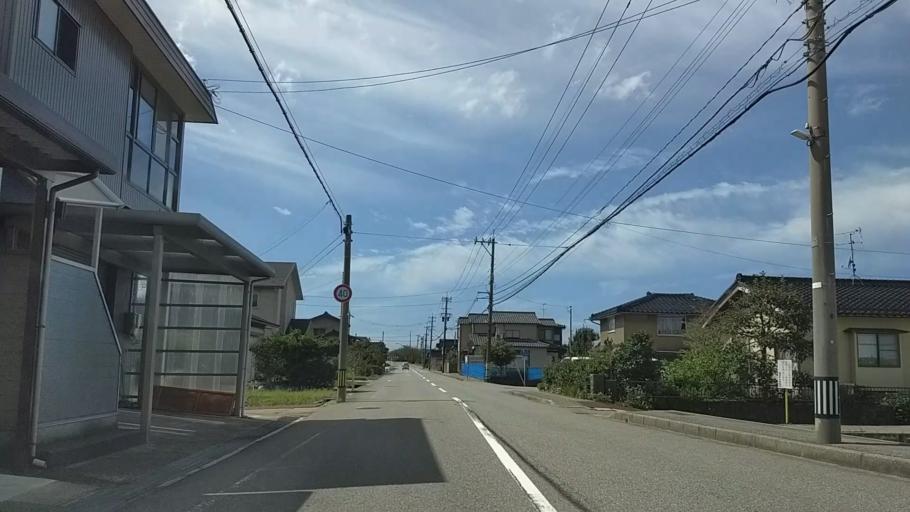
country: JP
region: Ishikawa
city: Kanazawa-shi
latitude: 36.5953
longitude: 136.6545
